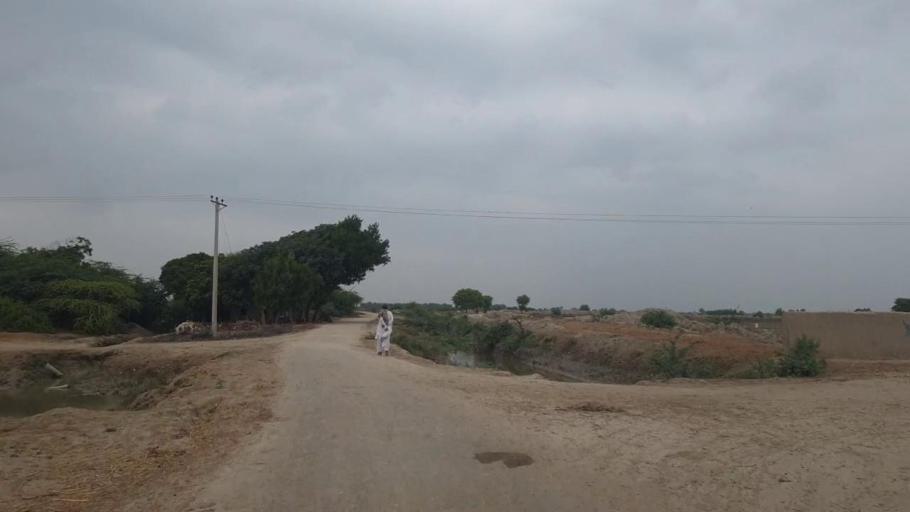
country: PK
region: Sindh
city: Badin
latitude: 24.6323
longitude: 68.6818
